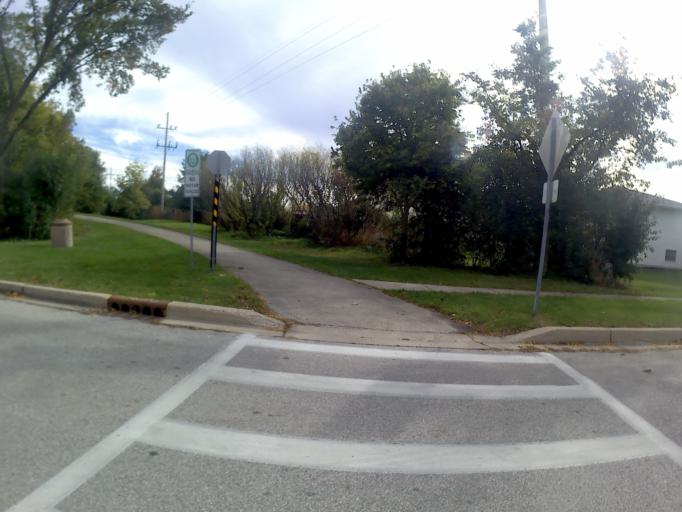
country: US
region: Illinois
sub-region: DuPage County
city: West Chicago
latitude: 41.9219
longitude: -88.2099
